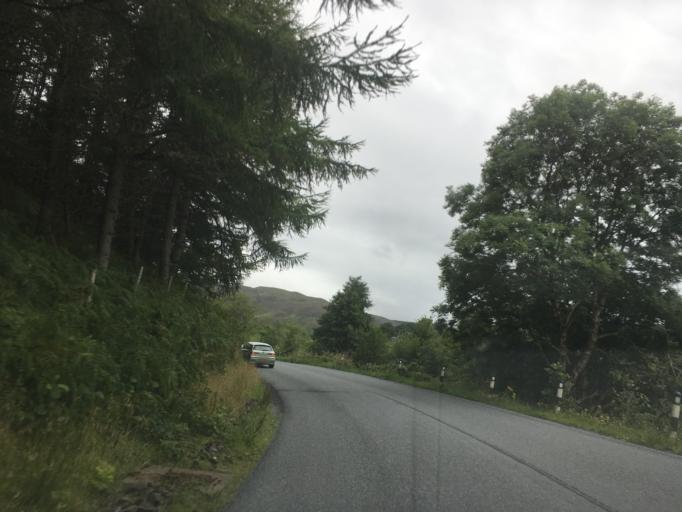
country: GB
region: Scotland
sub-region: Argyll and Bute
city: Oban
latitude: 56.2674
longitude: -5.4796
